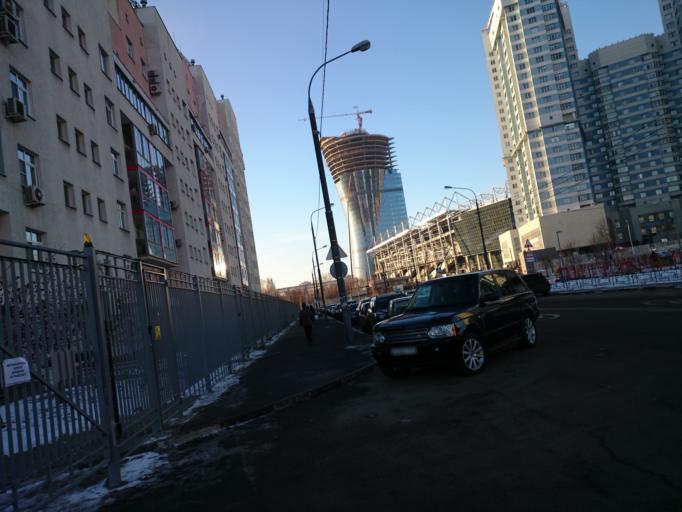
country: RU
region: Moscow
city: Sokol
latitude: 55.7895
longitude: 37.5219
